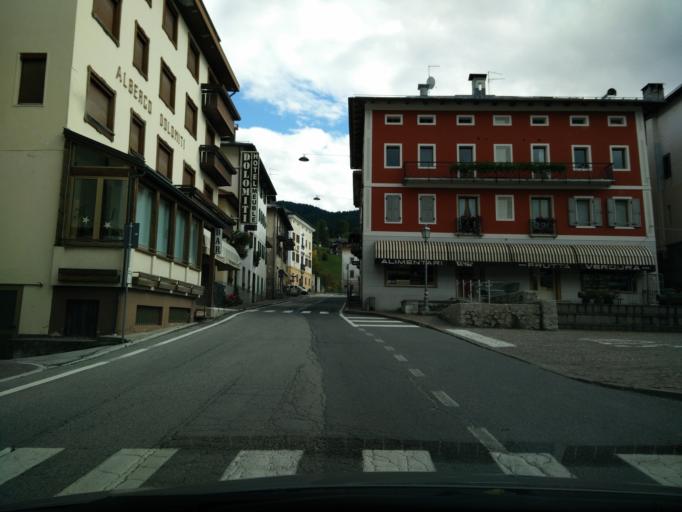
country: IT
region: Veneto
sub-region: Provincia di Belluno
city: Lorenzago di Cadore
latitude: 46.4804
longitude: 12.4585
